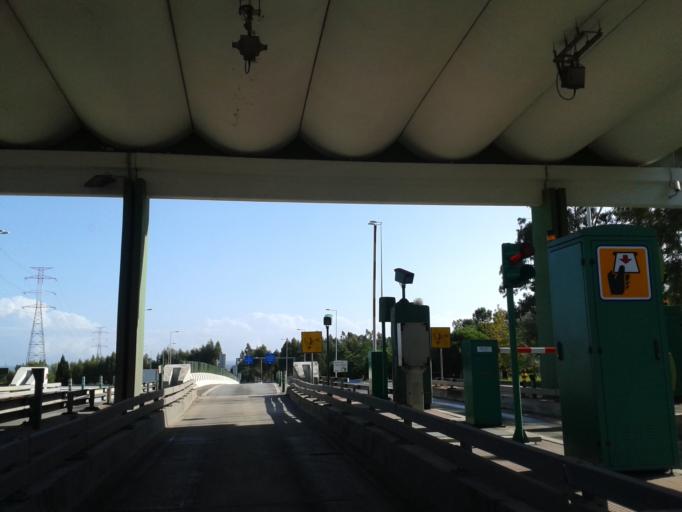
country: PT
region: Setubal
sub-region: Palmela
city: Palmela
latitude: 38.5844
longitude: -8.8887
